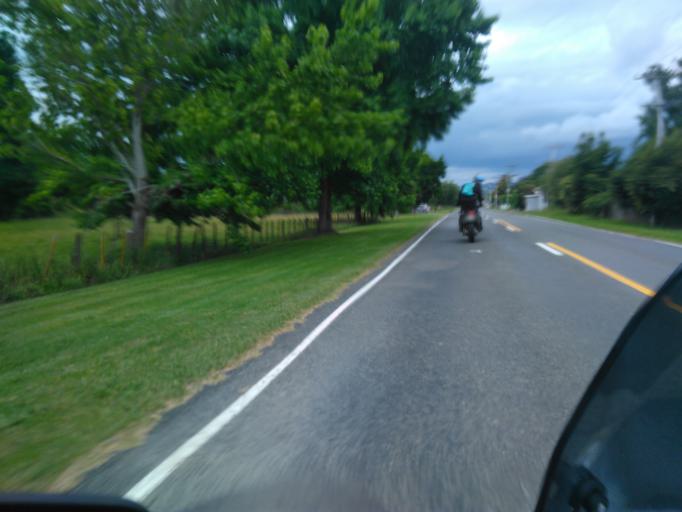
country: NZ
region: Gisborne
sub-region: Gisborne District
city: Gisborne
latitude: -38.4734
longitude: 177.8627
